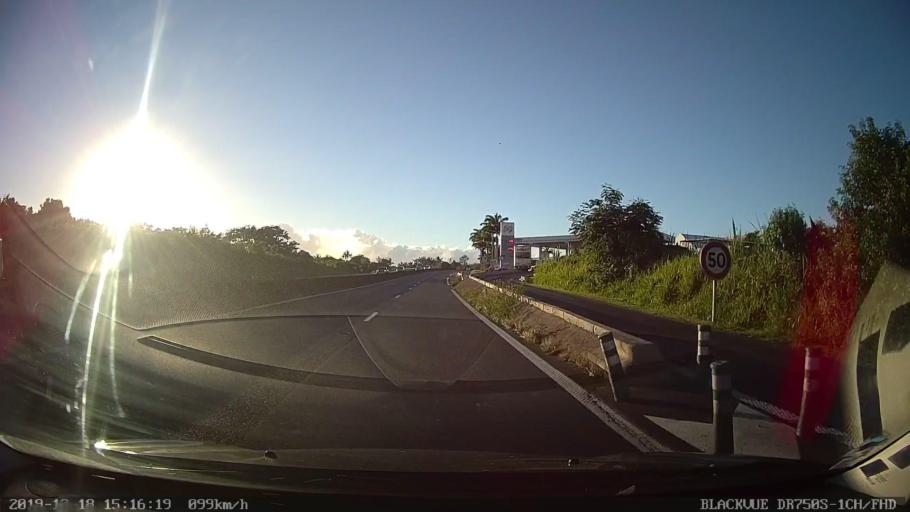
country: RE
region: Reunion
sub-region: Reunion
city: Saint-Andre
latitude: -20.9501
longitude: 55.6541
